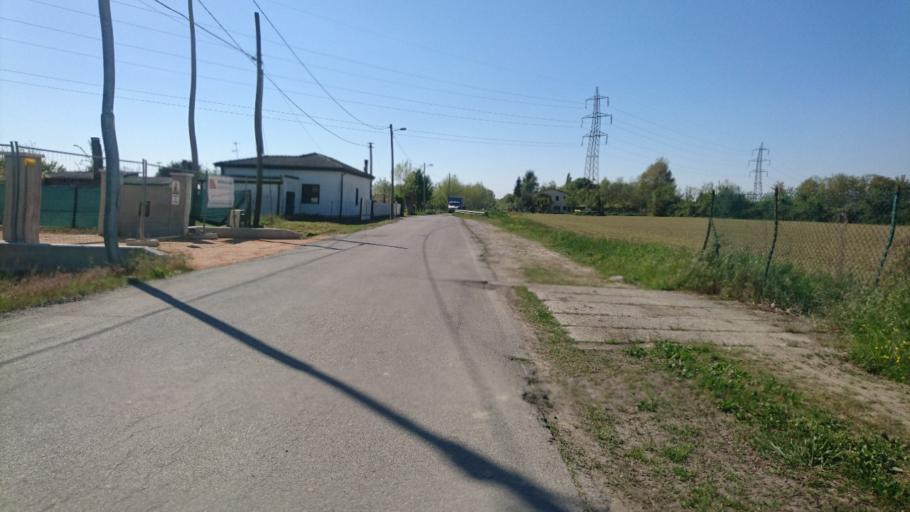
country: IT
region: Veneto
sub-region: Provincia di Venezia
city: Dese
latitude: 45.5181
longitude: 12.2642
